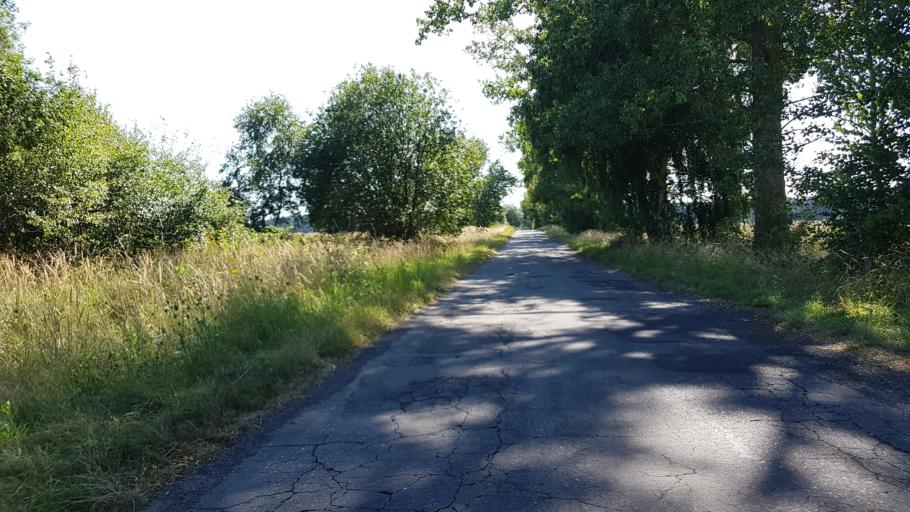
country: PL
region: West Pomeranian Voivodeship
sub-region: Powiat gryfinski
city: Gryfino
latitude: 53.1671
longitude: 14.5327
